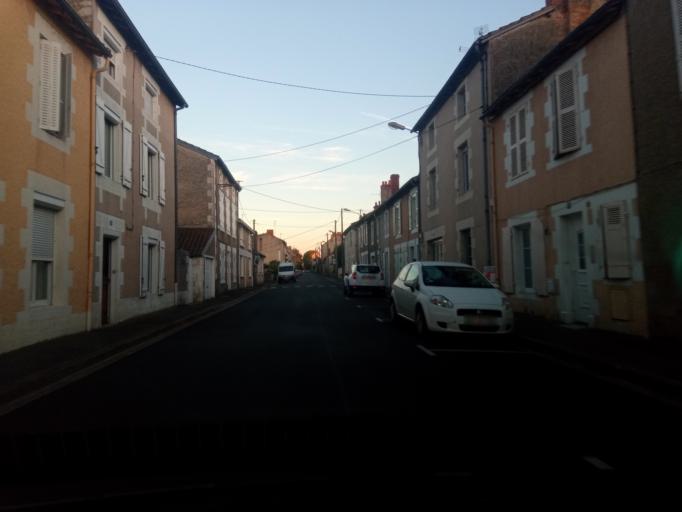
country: FR
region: Poitou-Charentes
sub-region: Departement de la Vienne
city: Montmorillon
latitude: 46.4215
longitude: 0.8690
